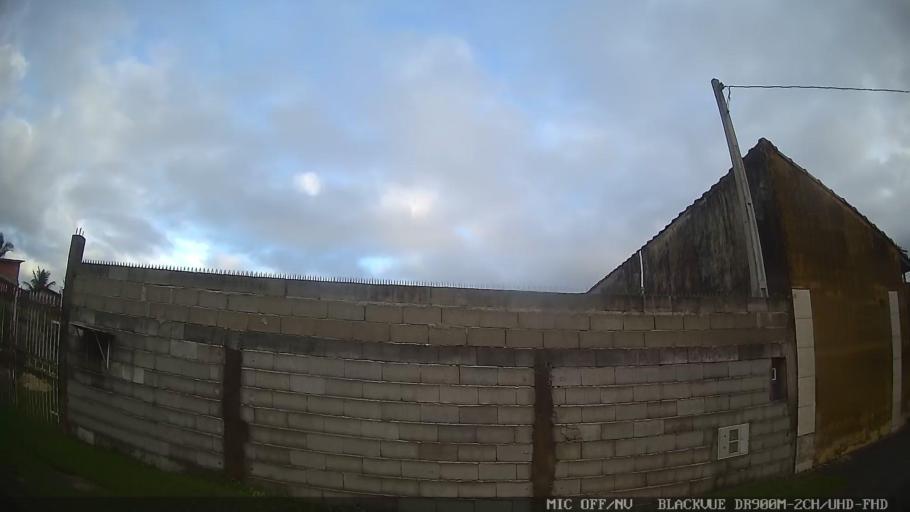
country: BR
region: Sao Paulo
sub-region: Itanhaem
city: Itanhaem
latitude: -24.2328
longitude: -46.8820
